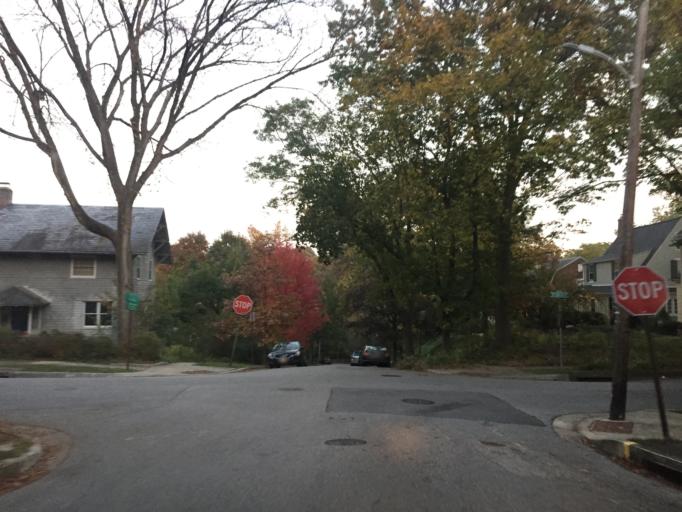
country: US
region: Maryland
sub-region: Baltimore County
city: Towson
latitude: 39.3486
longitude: -76.6304
